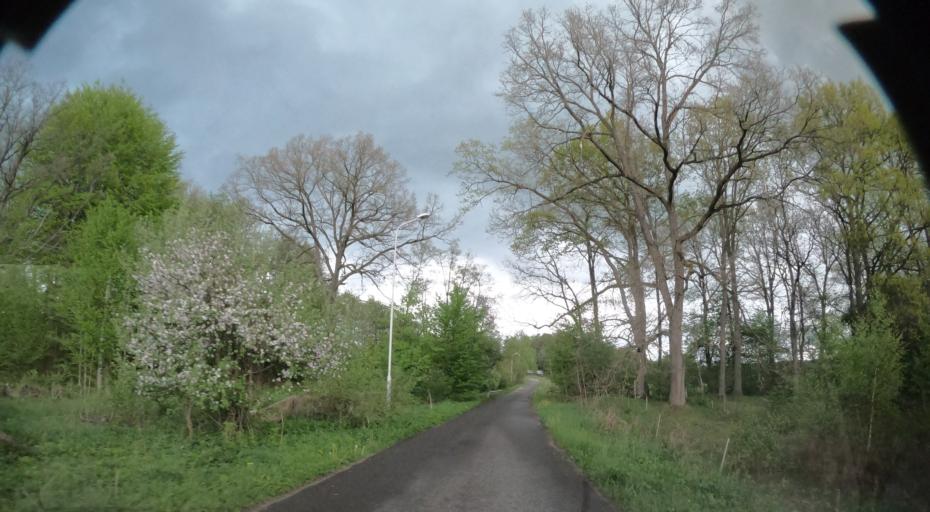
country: PL
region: West Pomeranian Voivodeship
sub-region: Powiat koszalinski
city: Bobolice
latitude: 54.1161
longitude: 16.5012
